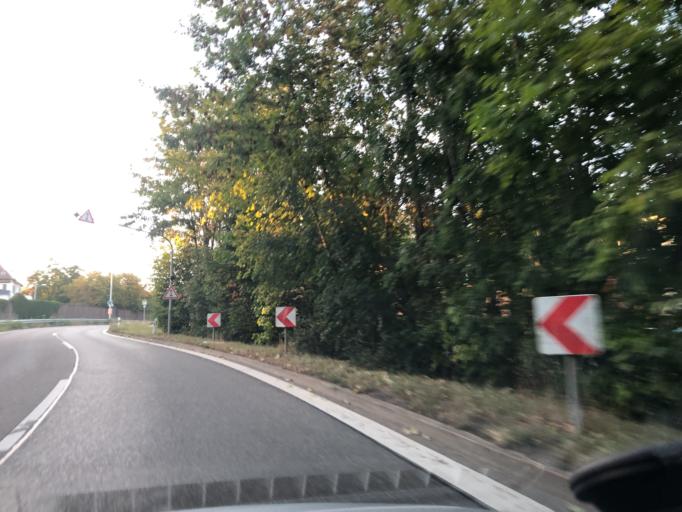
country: DE
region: Baden-Wuerttemberg
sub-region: Regierungsbezirk Stuttgart
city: Ludwigsburg
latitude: 48.8828
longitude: 9.1953
